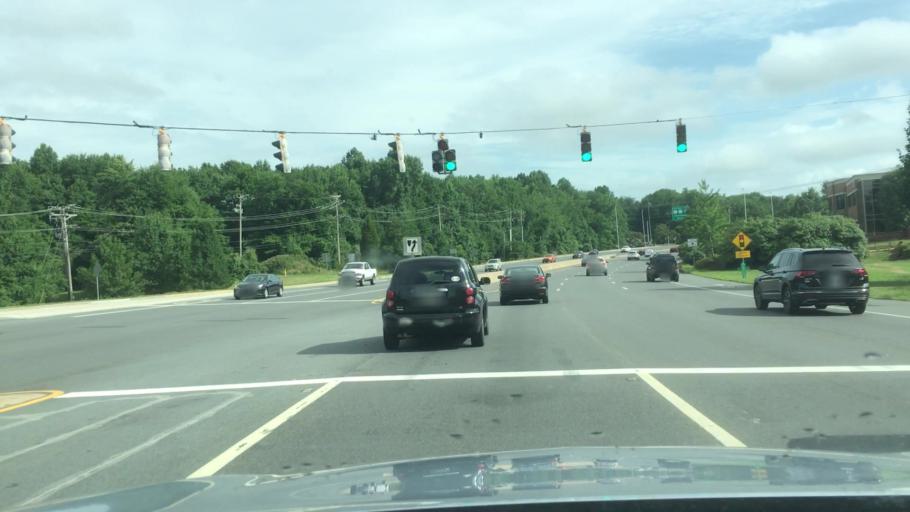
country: US
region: Delaware
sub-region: New Castle County
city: Newport
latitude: 39.7000
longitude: -75.6516
